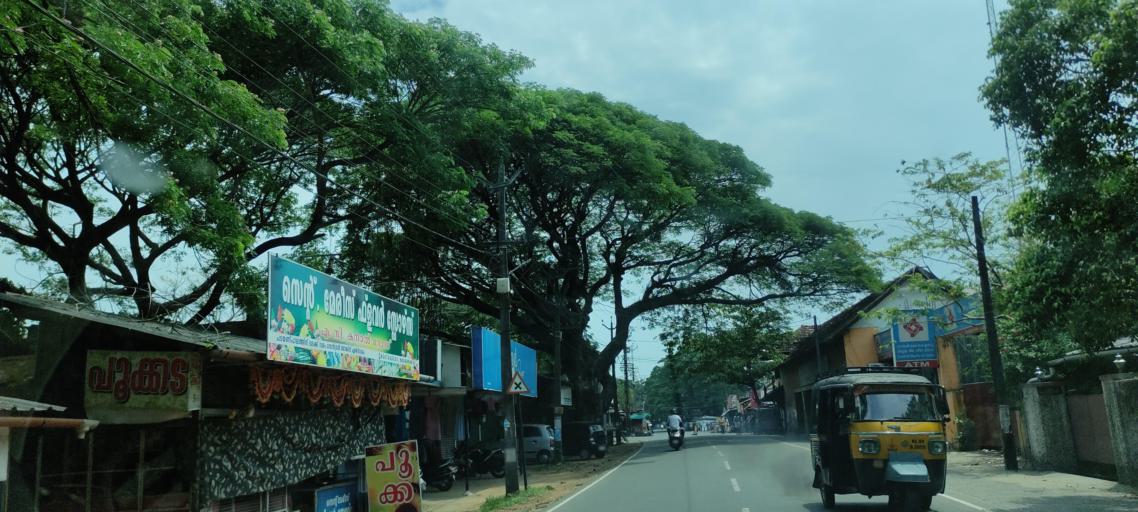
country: IN
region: Kerala
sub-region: Alappuzha
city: Shertallai
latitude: 9.6870
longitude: 76.3398
